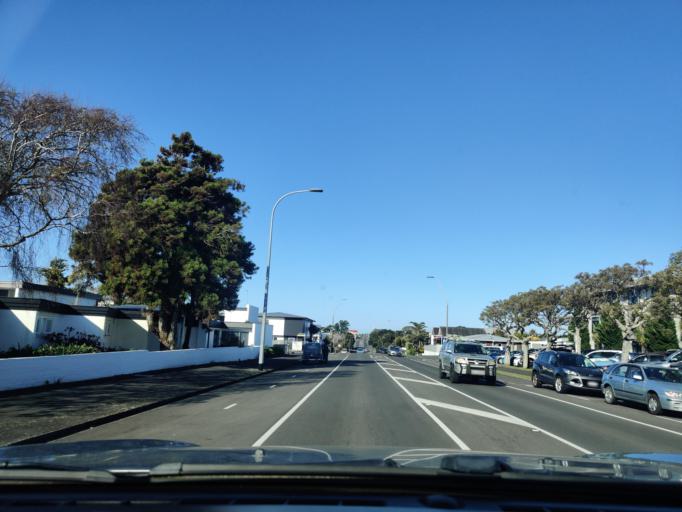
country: NZ
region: Taranaki
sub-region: New Plymouth District
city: New Plymouth
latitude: -39.0533
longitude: 174.0888
